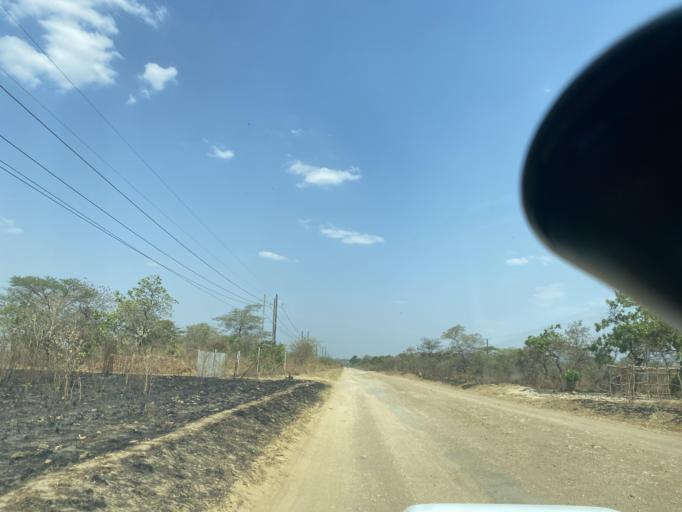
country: ZM
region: Lusaka
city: Lusaka
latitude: -15.3138
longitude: 28.0547
